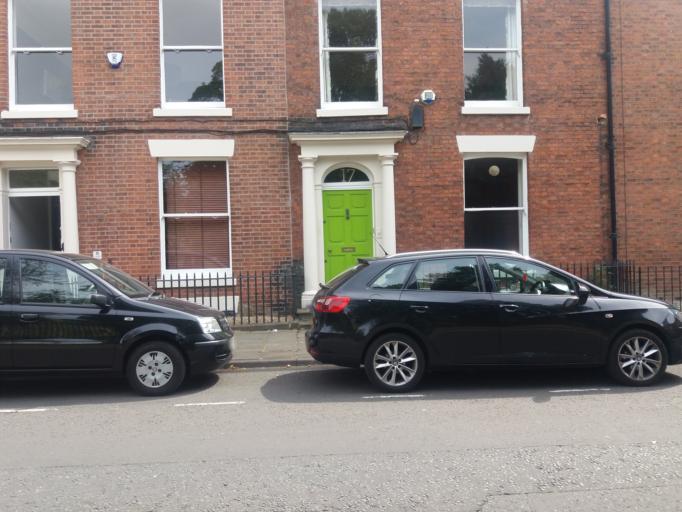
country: GB
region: England
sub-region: Lancashire
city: Preston
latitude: 53.7554
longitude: -2.7017
